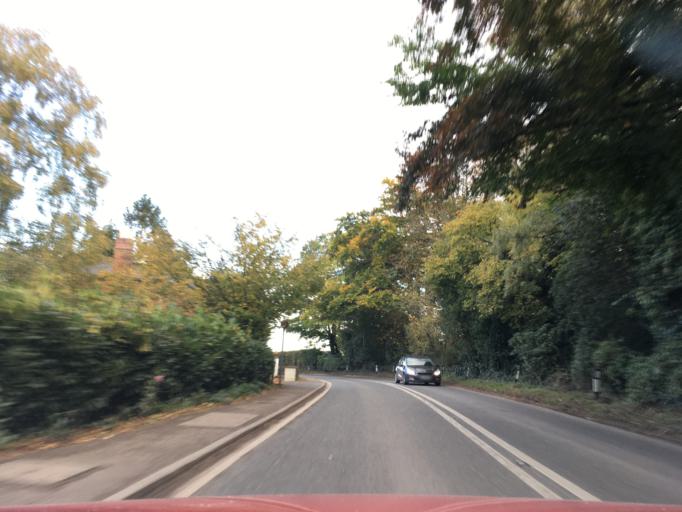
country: GB
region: England
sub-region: Herefordshire
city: Ocle Pychard
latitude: 52.0650
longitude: -2.5561
